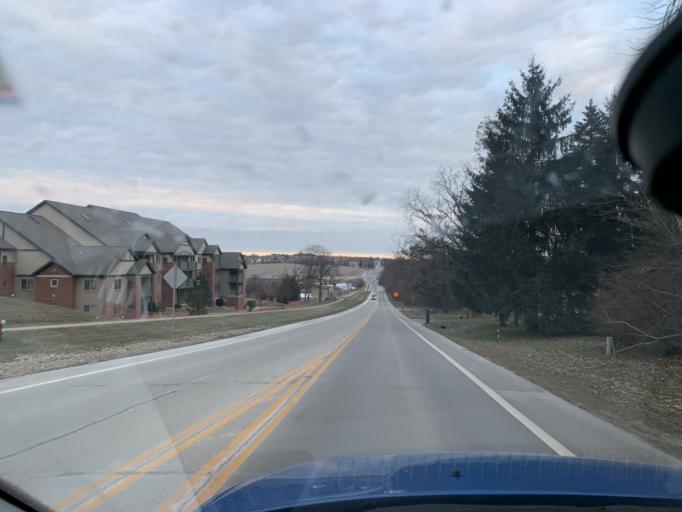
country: US
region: Wisconsin
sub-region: Dane County
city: Verona
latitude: 43.0312
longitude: -89.5431
